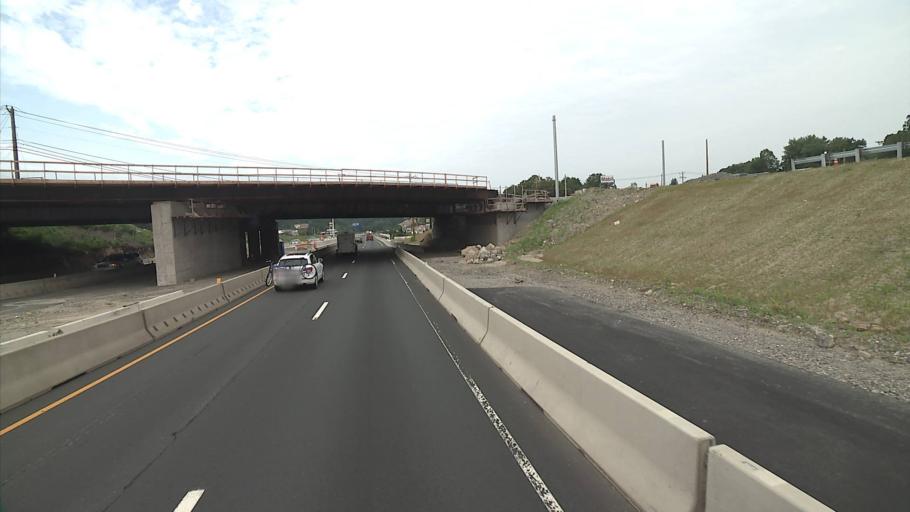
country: US
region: Connecticut
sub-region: New Haven County
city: Prospect
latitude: 41.5411
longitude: -72.9942
